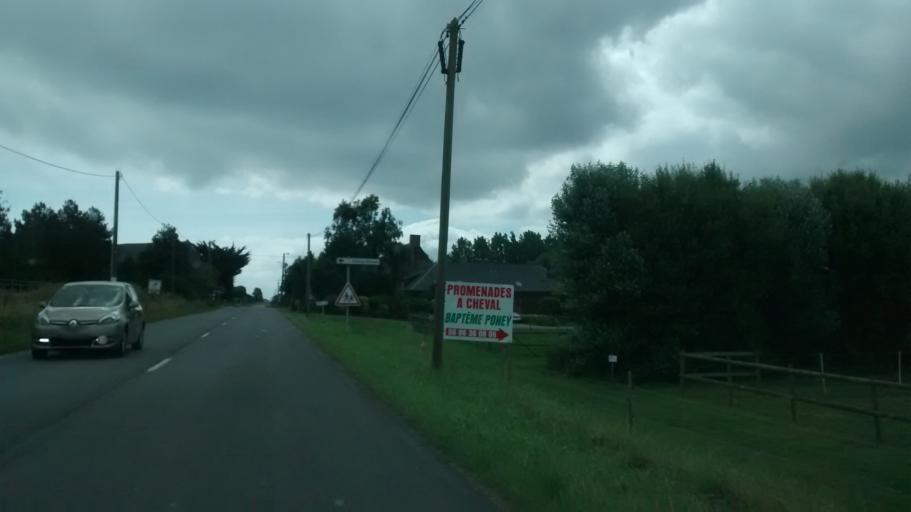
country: FR
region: Brittany
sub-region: Departement d'Ille-et-Vilaine
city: Saint-Meloir-des-Ondes
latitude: 48.6418
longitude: -1.8768
